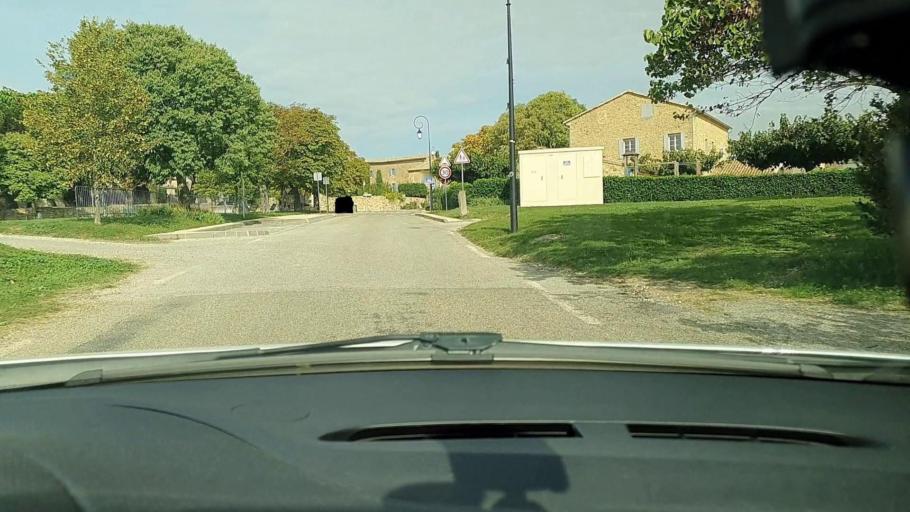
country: FR
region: Languedoc-Roussillon
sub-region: Departement du Gard
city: Saint-Quentin-la-Poterie
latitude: 44.1103
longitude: 4.4151
